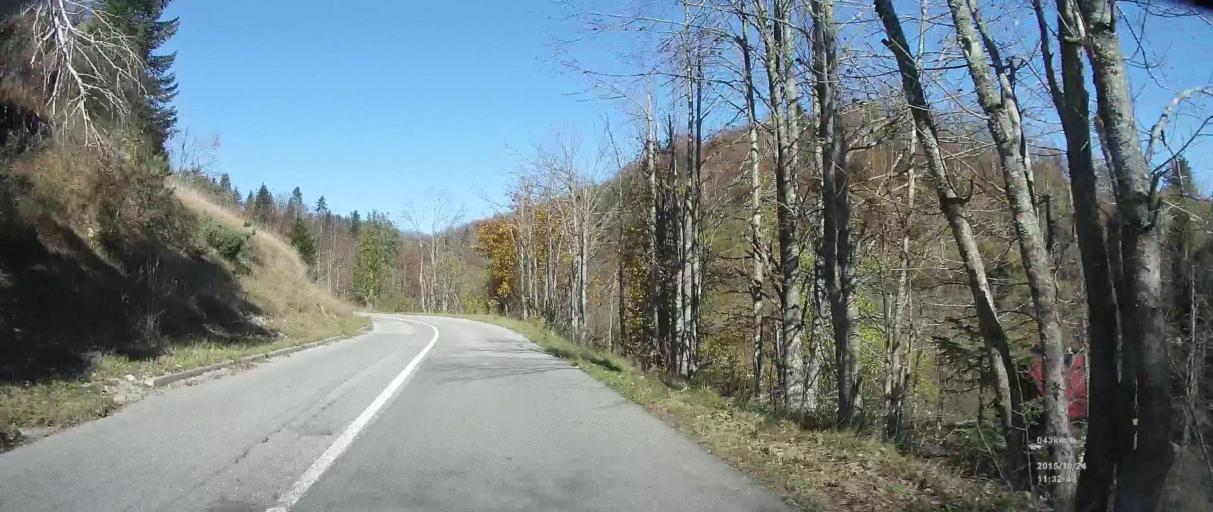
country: HR
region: Primorsko-Goranska
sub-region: Grad Delnice
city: Delnice
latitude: 45.3908
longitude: 14.6864
